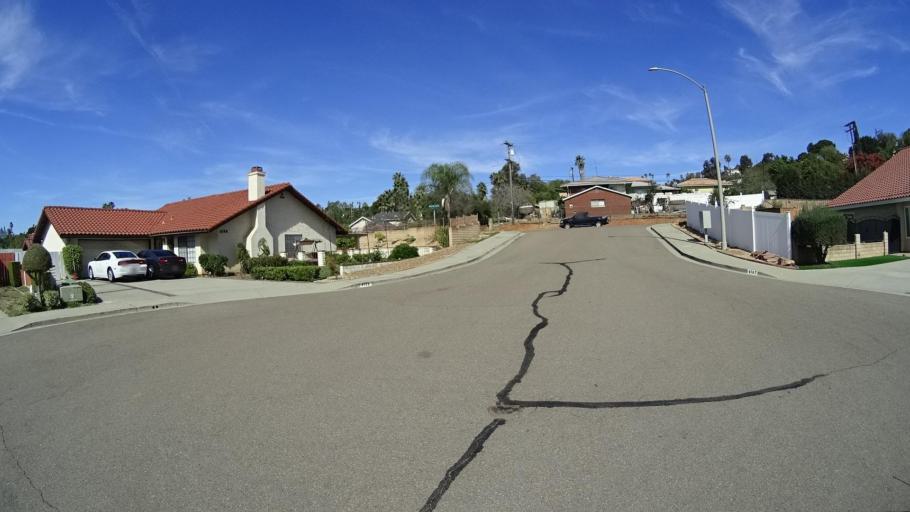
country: US
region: California
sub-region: San Diego County
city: Casa de Oro-Mount Helix
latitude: 32.7545
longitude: -116.9604
